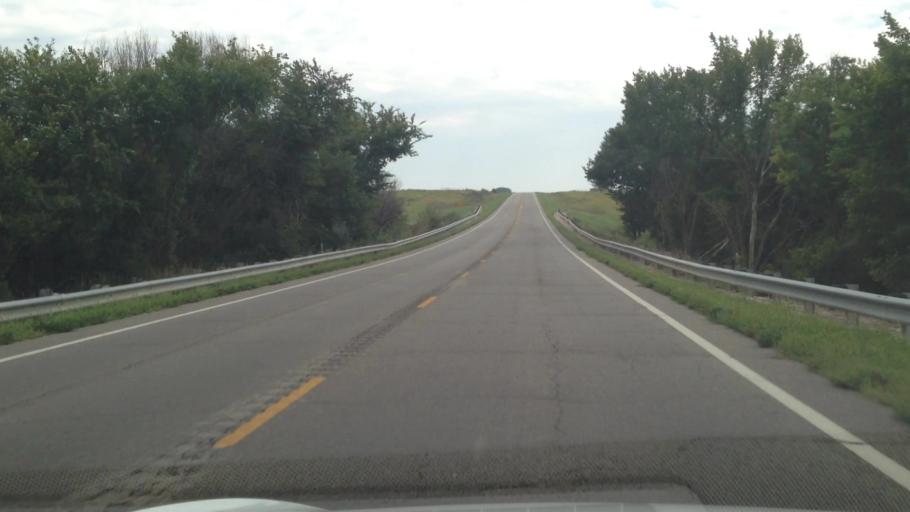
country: US
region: Kansas
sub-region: Bourbon County
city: Fort Scott
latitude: 37.8866
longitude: -95.0260
